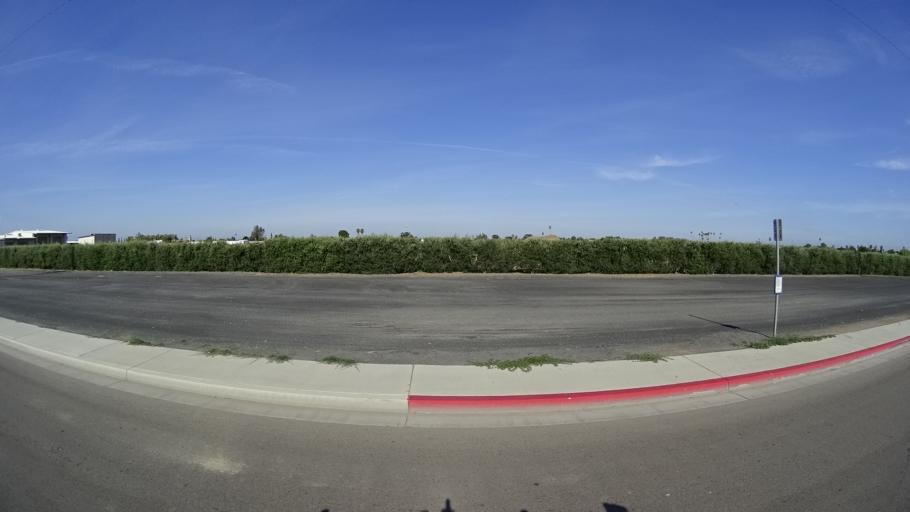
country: US
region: California
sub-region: Kings County
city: Home Garden
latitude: 36.3166
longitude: -119.6371
